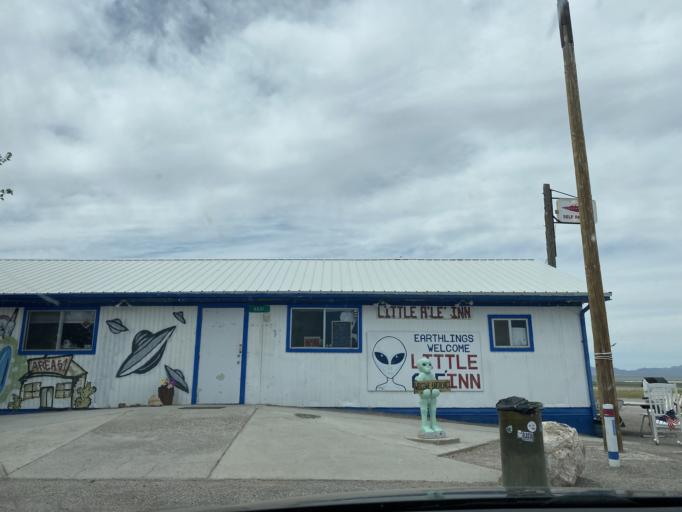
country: US
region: Nevada
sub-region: Lincoln County
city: Alamo
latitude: 37.6467
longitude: -115.7458
